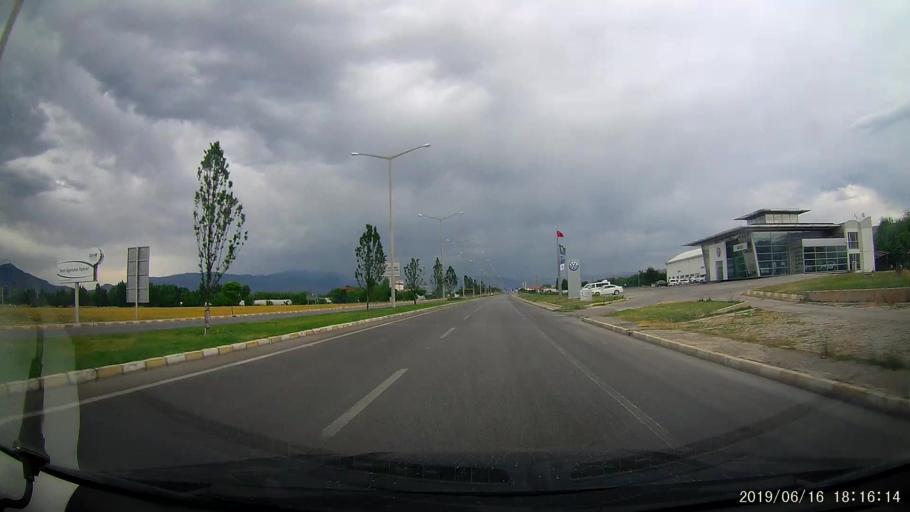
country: TR
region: Erzincan
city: Erzincan
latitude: 39.7272
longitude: 39.5506
